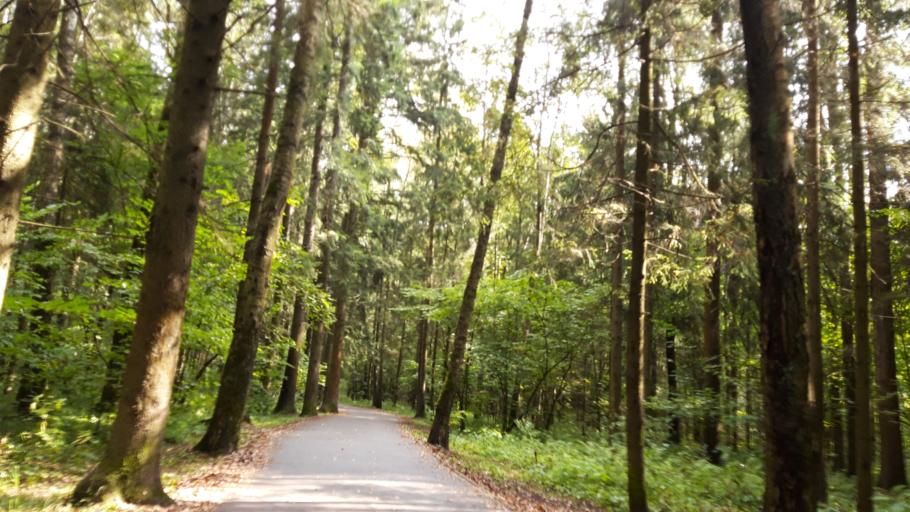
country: RU
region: Moscow
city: Zelenograd
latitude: 55.9837
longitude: 37.1999
